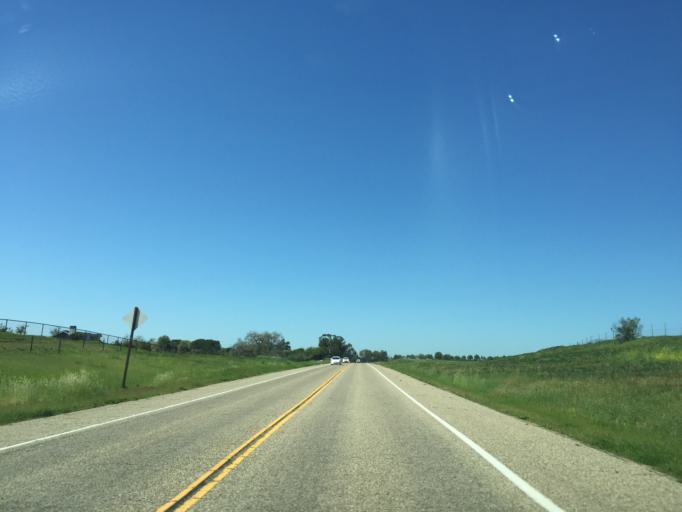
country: US
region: California
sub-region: Santa Barbara County
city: Santa Ynez
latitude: 34.6247
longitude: -120.0719
